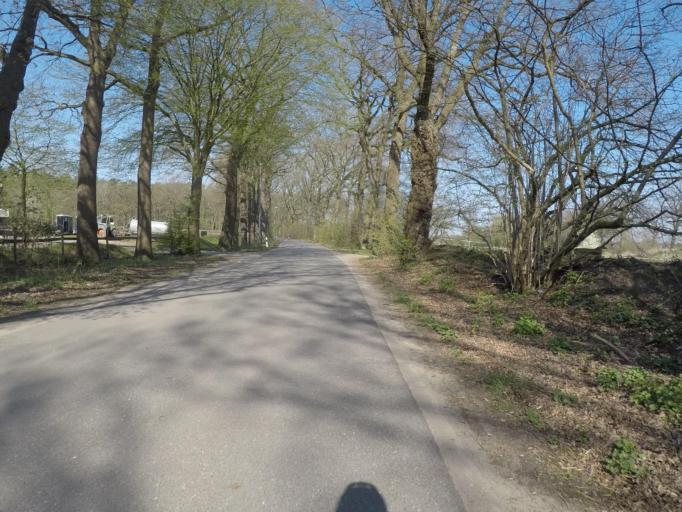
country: DE
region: Schleswig-Holstein
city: Rellingen
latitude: 53.6063
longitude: 9.8016
